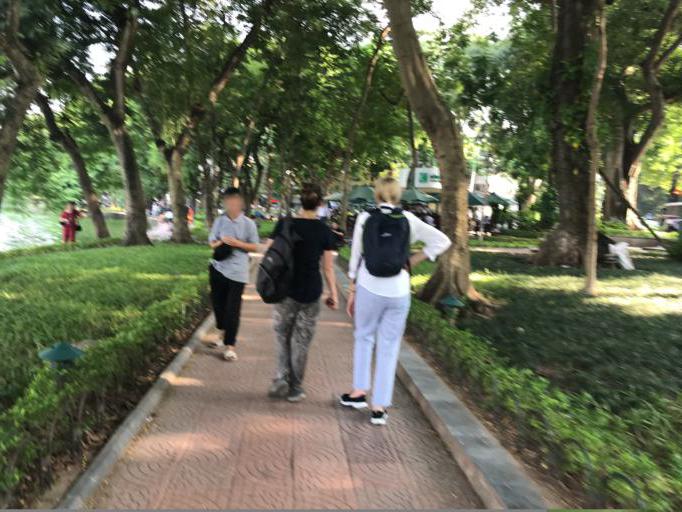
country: VN
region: Ha Noi
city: Hoan Kiem
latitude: 21.0268
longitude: 105.8517
